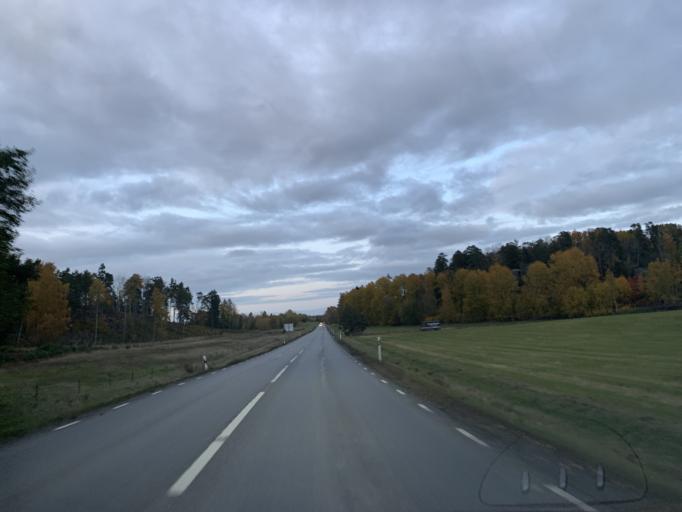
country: SE
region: Stockholm
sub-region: Nynashamns Kommun
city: Osmo
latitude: 58.9976
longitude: 17.7986
